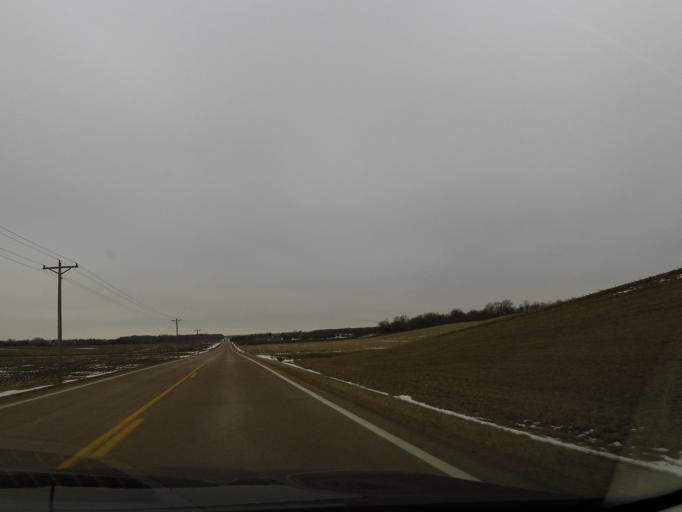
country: US
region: Minnesota
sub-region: Carver County
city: Carver
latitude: 44.7533
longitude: -93.6839
